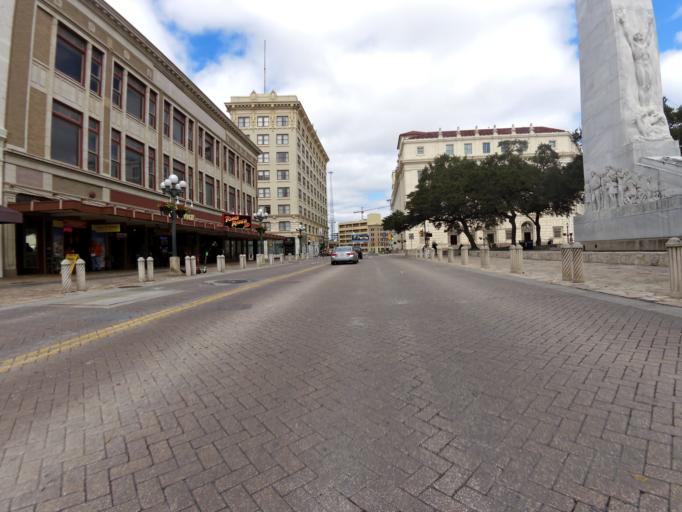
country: US
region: Texas
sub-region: Bexar County
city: San Antonio
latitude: 29.4260
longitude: -98.4869
